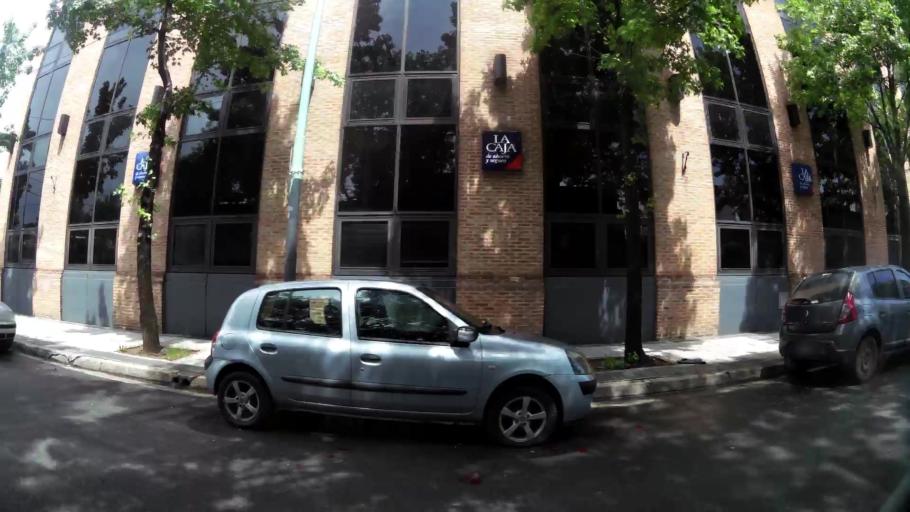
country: AR
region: Buenos Aires F.D.
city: Colegiales
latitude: -34.5900
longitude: -58.4435
